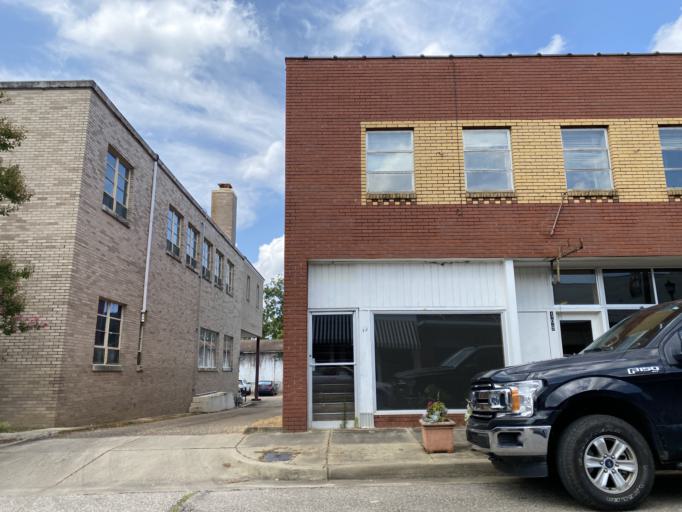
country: US
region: Alabama
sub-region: Wilcox County
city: Camden
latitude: 31.9914
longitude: -87.2896
